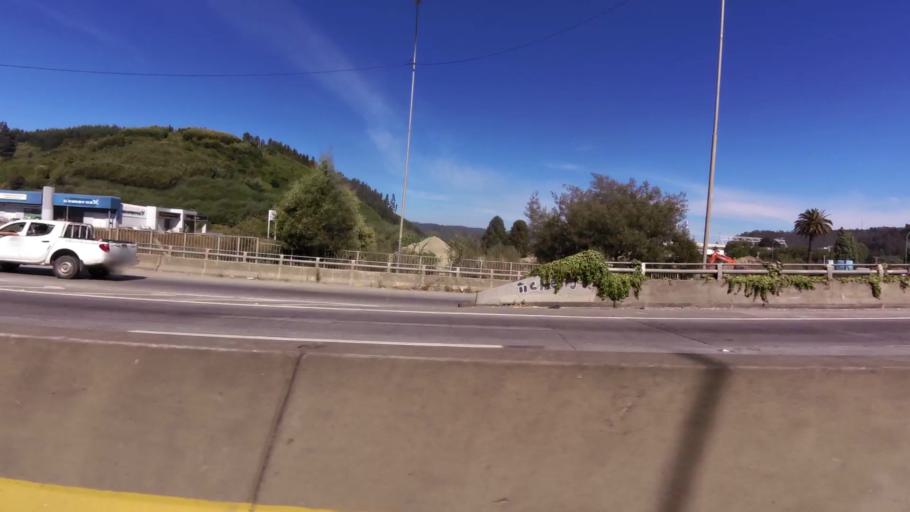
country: CL
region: Biobio
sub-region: Provincia de Concepcion
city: Concepcion
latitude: -36.8100
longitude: -73.0267
